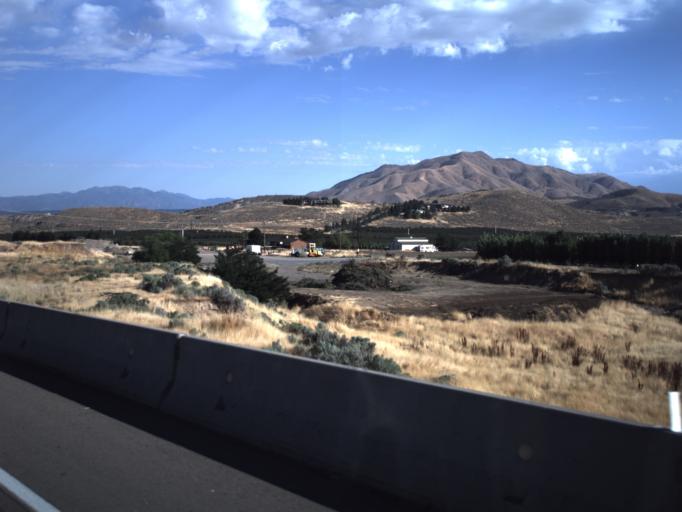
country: US
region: Utah
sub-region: Utah County
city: Santaquin
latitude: 39.9811
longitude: -111.8047
